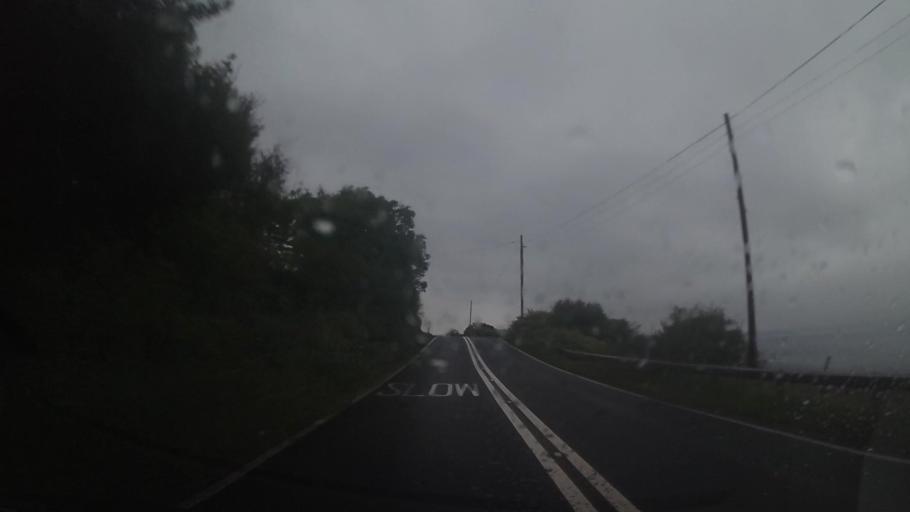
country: GB
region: Scotland
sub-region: North Ayrshire
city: Skelmorlie
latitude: 55.8404
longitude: -4.8918
